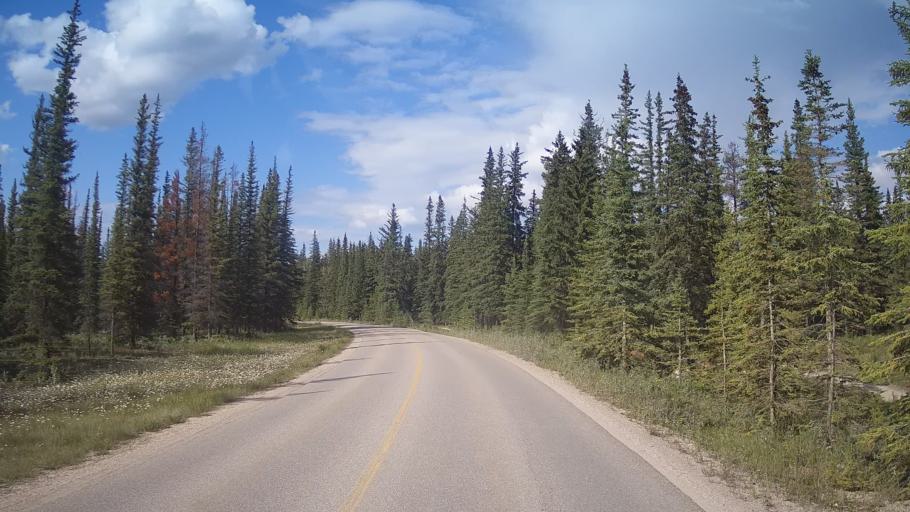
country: CA
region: Alberta
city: Jasper Park Lodge
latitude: 52.8621
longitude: -118.0707
